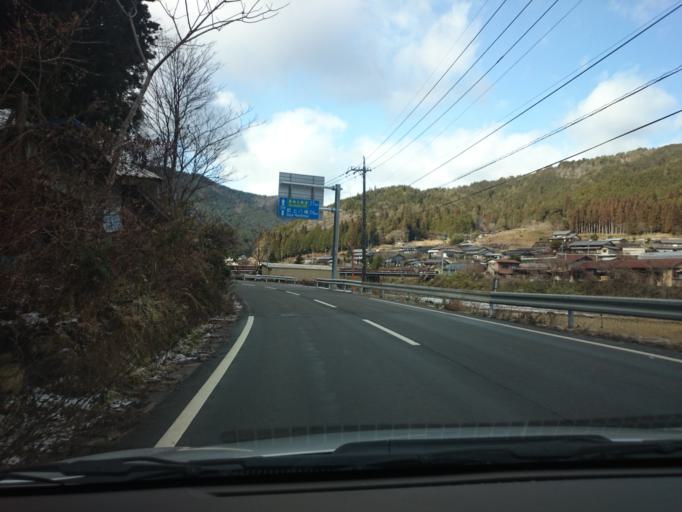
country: JP
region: Gifu
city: Gujo
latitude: 35.7413
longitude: 137.1197
